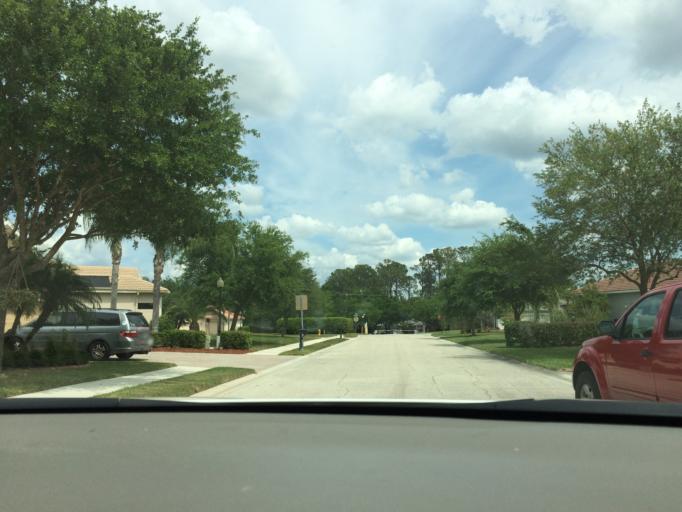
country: US
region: Florida
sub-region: Manatee County
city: Ellenton
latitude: 27.4899
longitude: -82.4105
